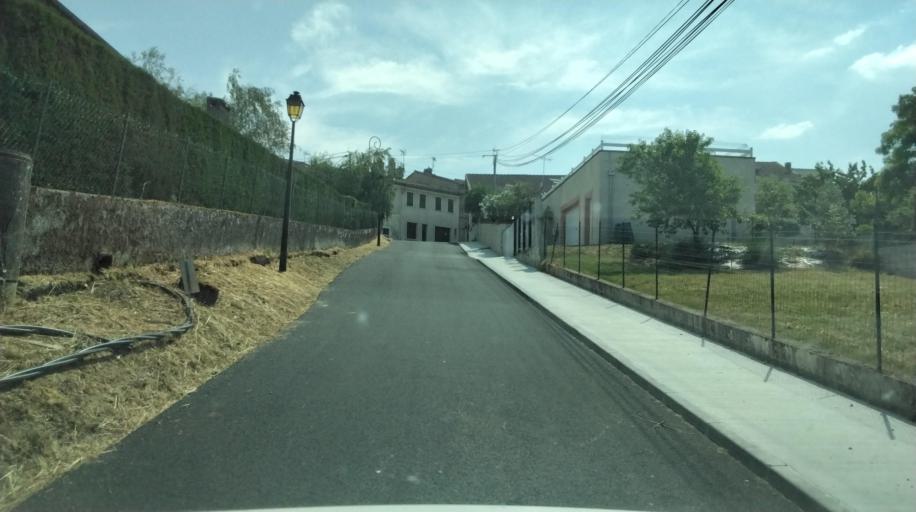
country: FR
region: Midi-Pyrenees
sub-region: Departement de la Haute-Garonne
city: Rieumes
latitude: 43.4132
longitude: 1.1242
